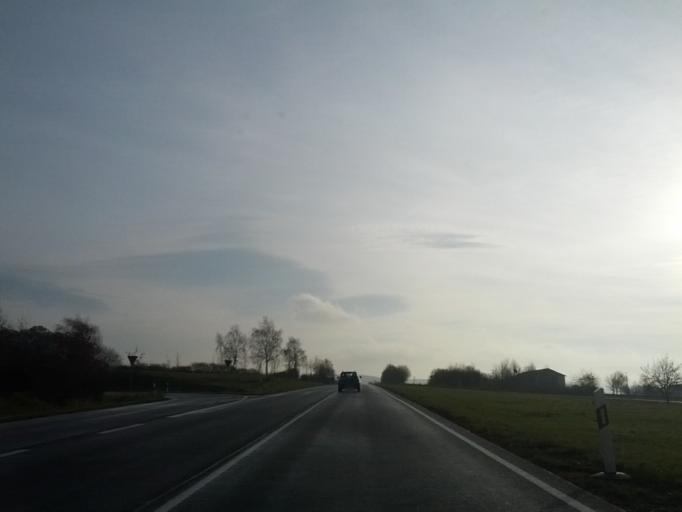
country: DE
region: Thuringia
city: Breitungen
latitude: 50.7708
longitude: 10.3289
